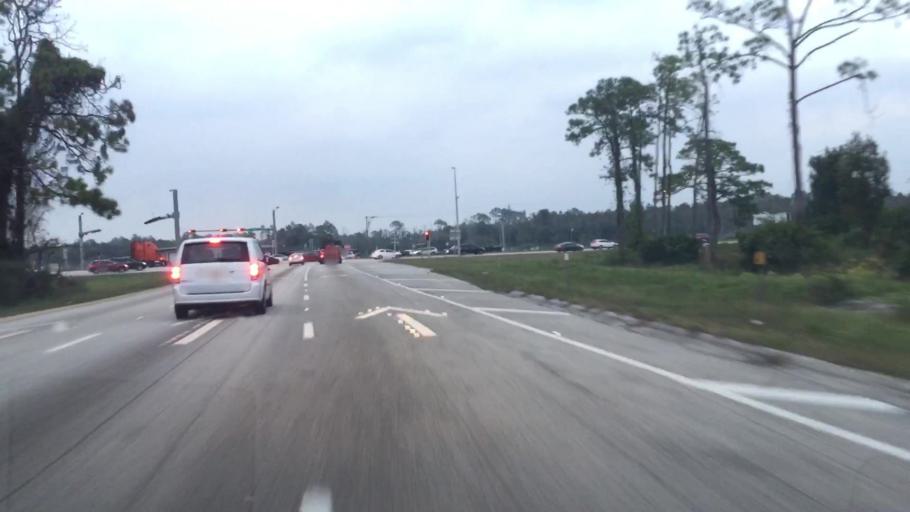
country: US
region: Florida
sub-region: Lee County
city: Fort Myers
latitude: 26.6335
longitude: -81.8023
